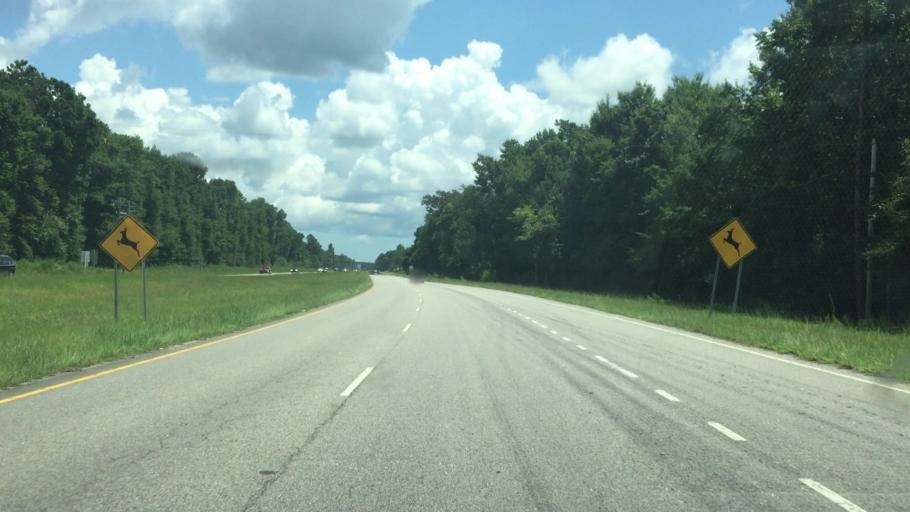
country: US
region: South Carolina
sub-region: Horry County
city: Loris
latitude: 34.0168
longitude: -78.7914
